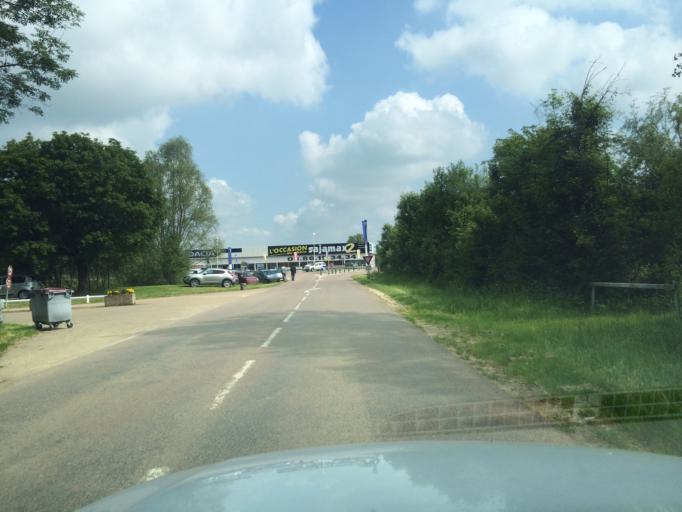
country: FR
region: Bourgogne
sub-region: Departement de l'Yonne
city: Laroche-Saint-Cydroine
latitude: 47.9557
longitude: 3.4484
